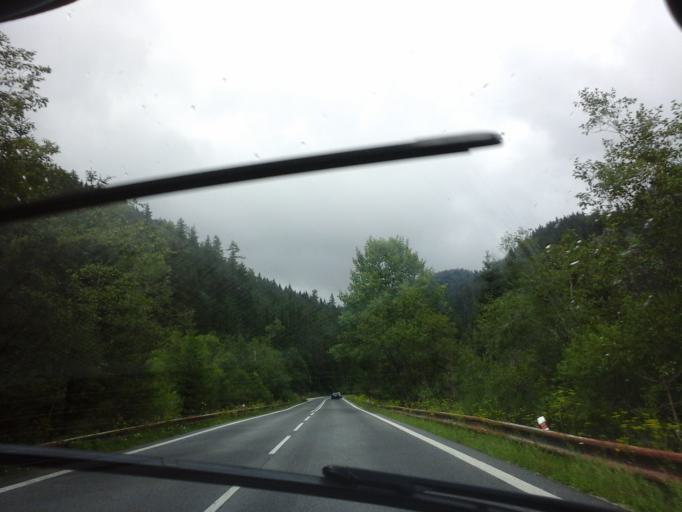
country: SK
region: Kosicky
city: Dobsina
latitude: 48.8791
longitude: 20.3191
